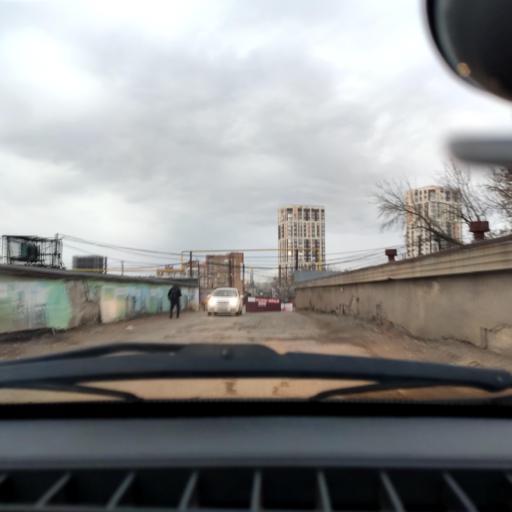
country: RU
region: Bashkortostan
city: Ufa
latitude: 54.7146
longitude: 55.9860
